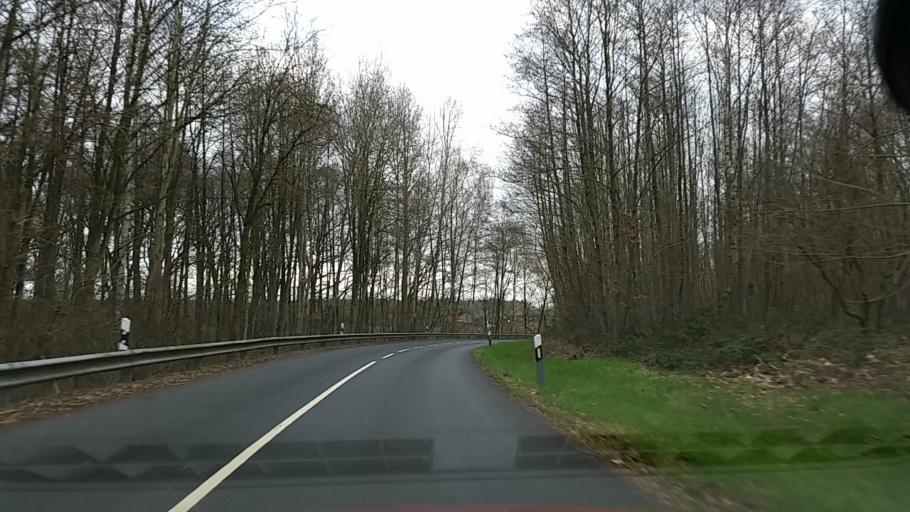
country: DE
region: Lower Saxony
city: Bodenteich
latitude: 52.8326
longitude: 10.6654
